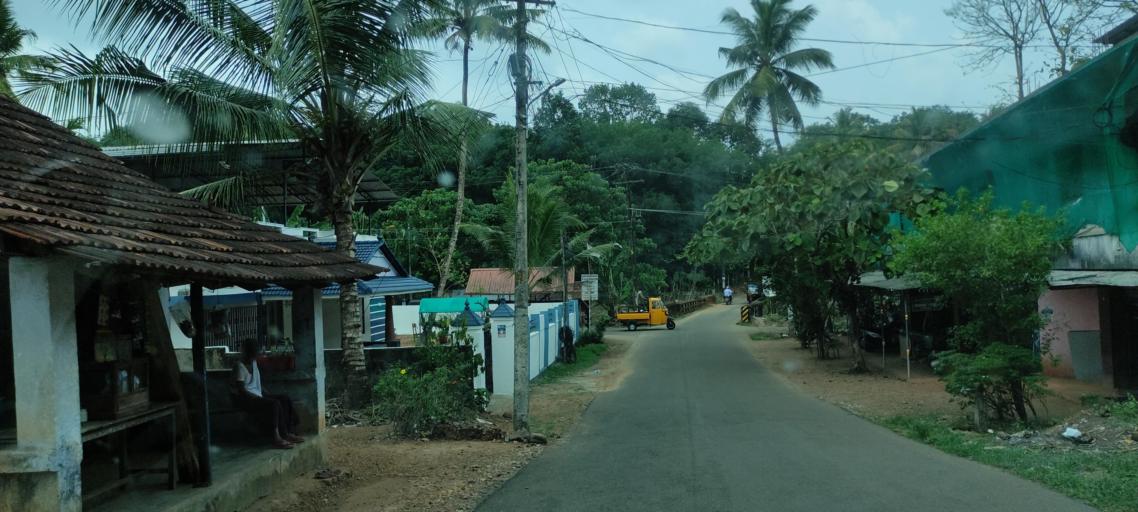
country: IN
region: Kerala
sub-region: Pattanamtitta
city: Adur
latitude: 9.1687
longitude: 76.7359
